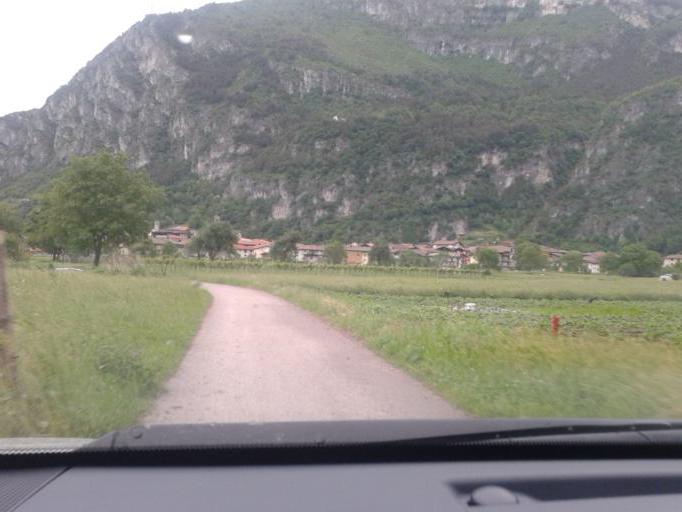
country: IT
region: Trentino-Alto Adige
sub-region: Provincia di Trento
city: Storo
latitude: 45.8442
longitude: 10.5765
